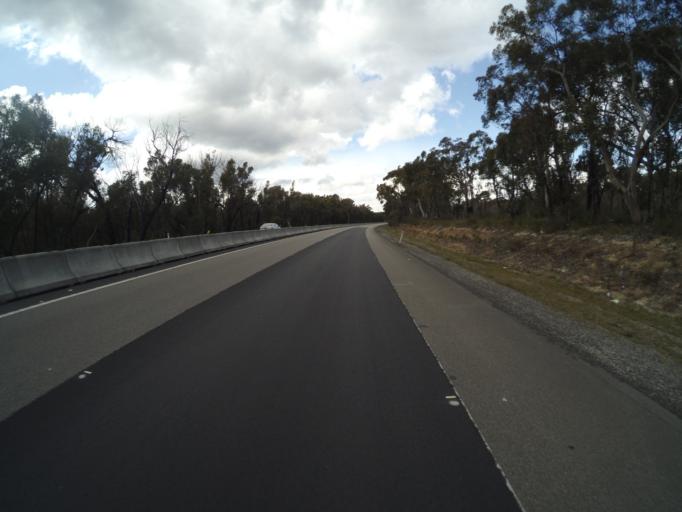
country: AU
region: New South Wales
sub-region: Wollongong
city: Mount Keira
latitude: -34.3235
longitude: 150.7707
